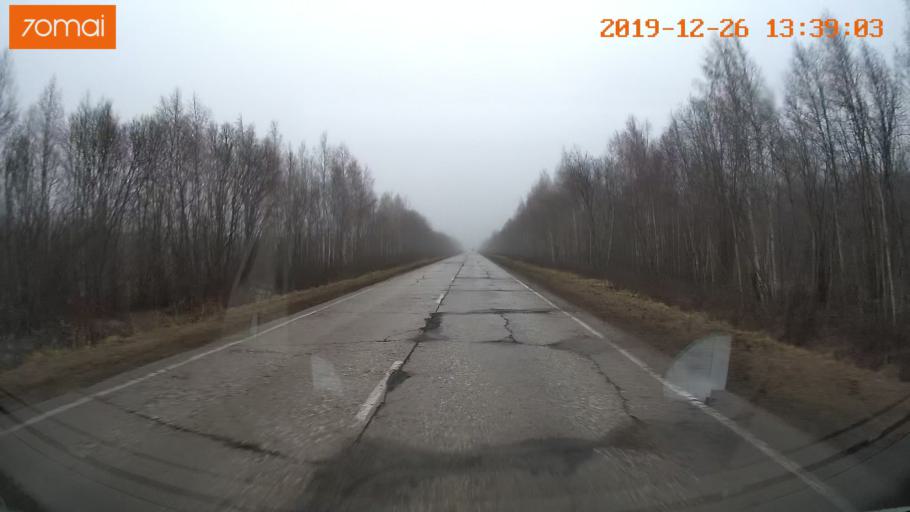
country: RU
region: Vologda
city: Sheksna
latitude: 58.7559
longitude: 38.4039
